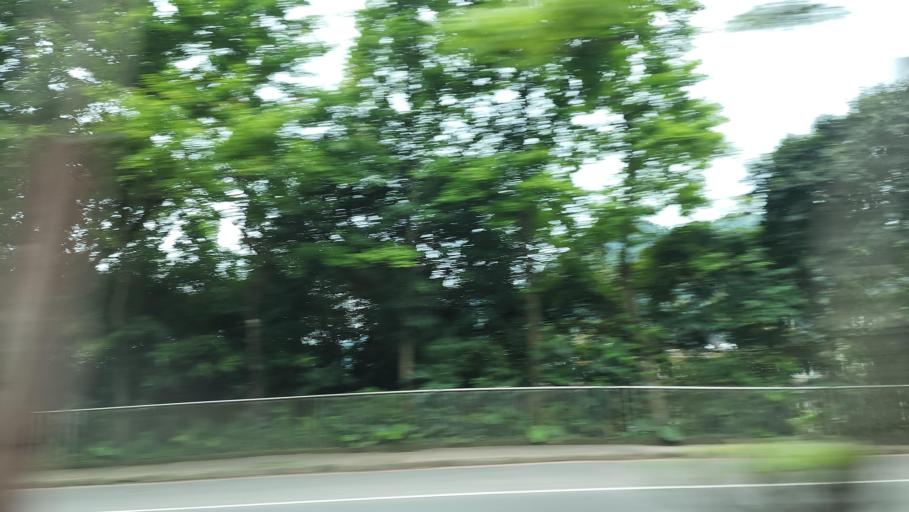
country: TW
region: Taiwan
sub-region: Keelung
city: Keelung
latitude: 25.1610
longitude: 121.6929
